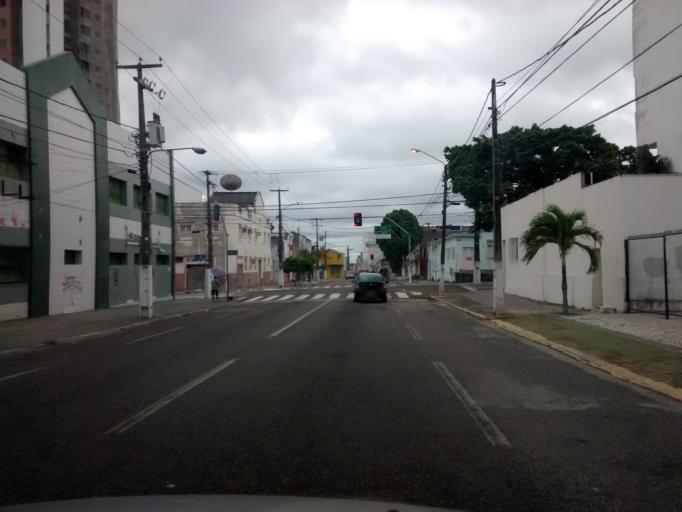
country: BR
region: Rio Grande do Norte
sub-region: Natal
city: Natal
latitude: -5.7891
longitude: -35.2069
